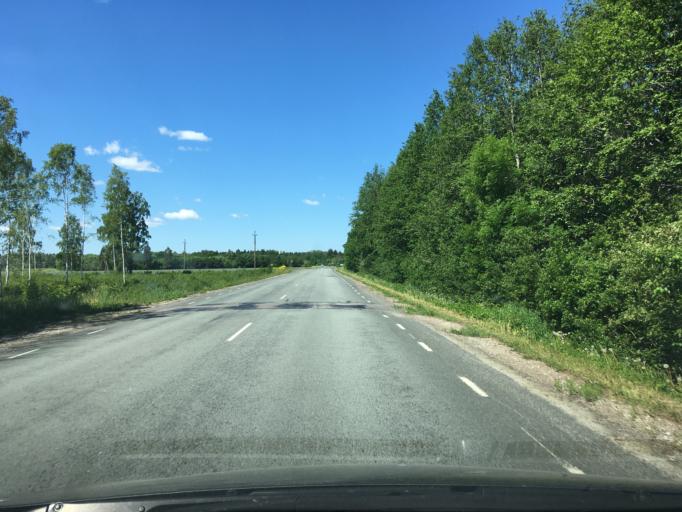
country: EE
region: Harju
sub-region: Rae vald
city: Vaida
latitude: 59.1930
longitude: 24.9959
